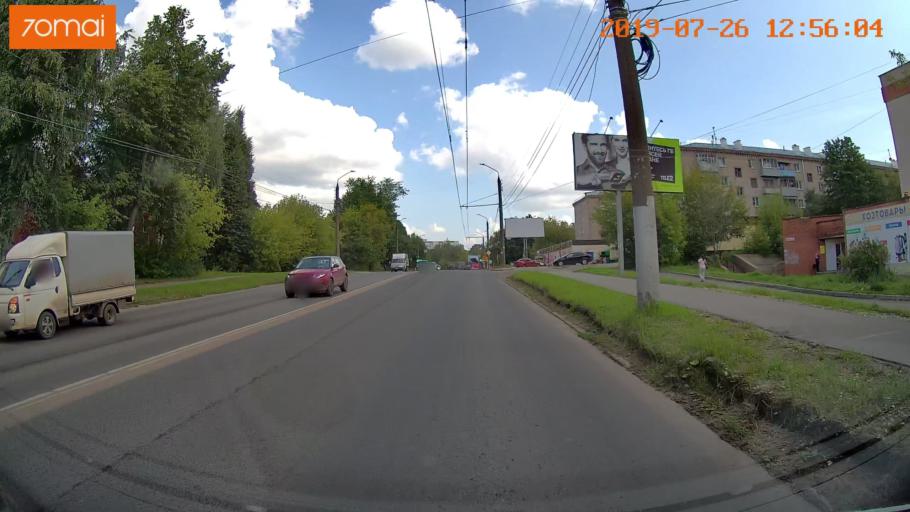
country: RU
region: Ivanovo
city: Bogorodskoye
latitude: 57.0165
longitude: 41.0070
